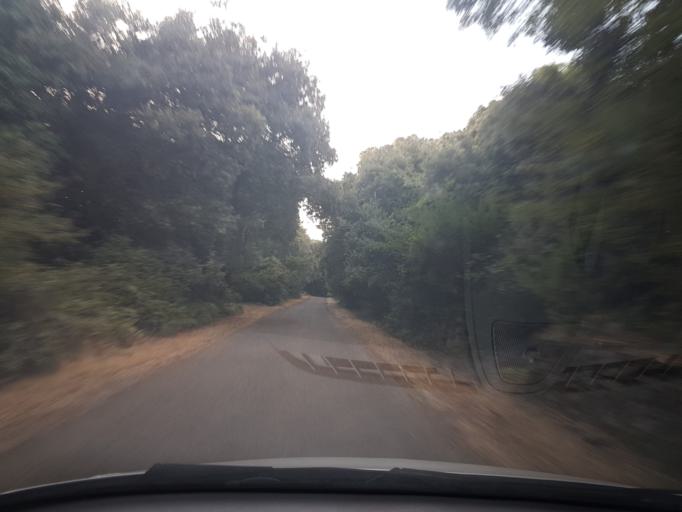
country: IT
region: Sardinia
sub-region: Provincia di Oristano
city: Seneghe
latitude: 40.1100
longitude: 8.5860
